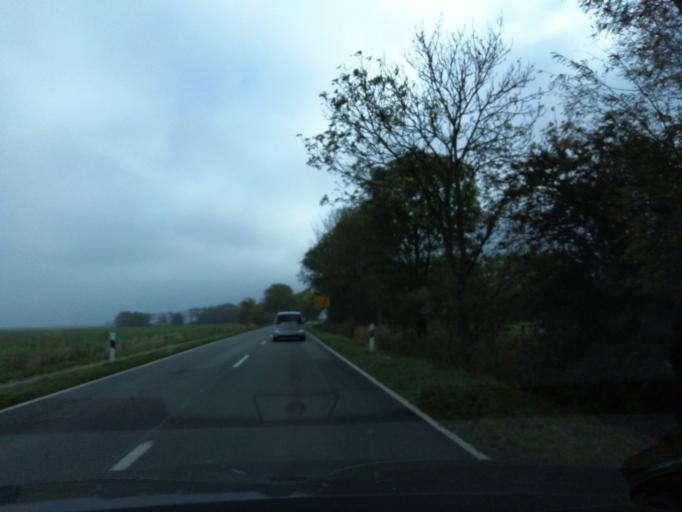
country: DE
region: Lower Saxony
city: Wangerooge
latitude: 53.6919
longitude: 7.8485
